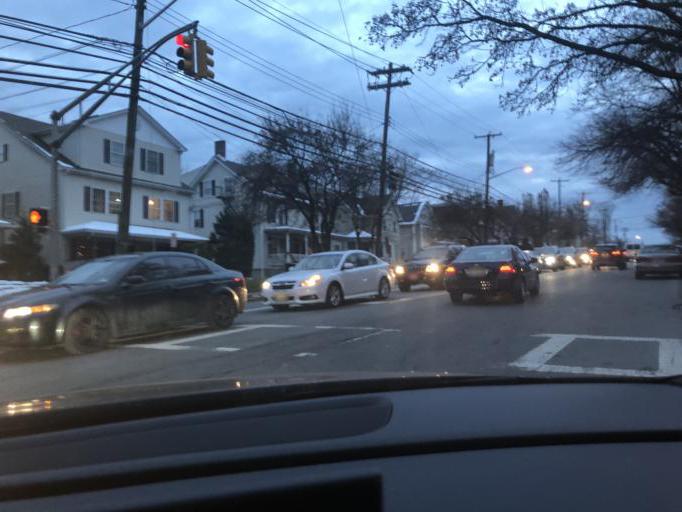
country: US
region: New Jersey
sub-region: Morris County
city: Morristown
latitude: 40.7991
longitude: -74.4690
